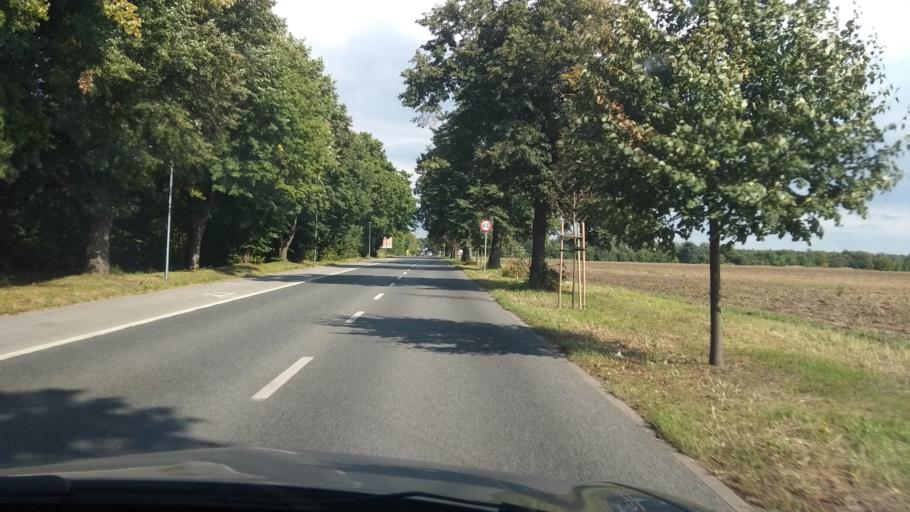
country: PL
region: Masovian Voivodeship
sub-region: Powiat pruszkowski
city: Komorow
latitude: 52.1573
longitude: 20.8304
